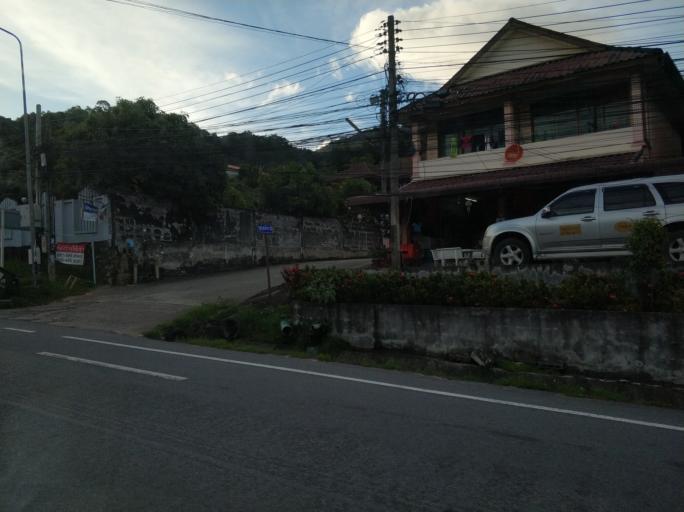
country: TH
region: Phuket
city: Kathu
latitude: 7.9052
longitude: 98.3267
